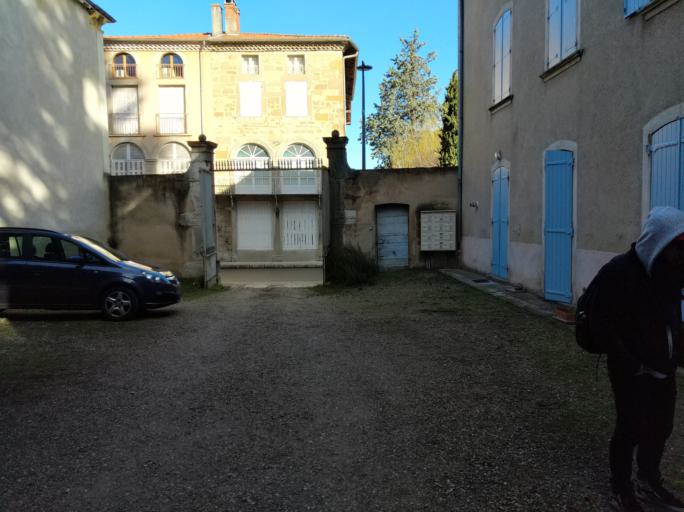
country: FR
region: Rhone-Alpes
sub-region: Departement de la Drome
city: Saint-Sorlin-en-Valloire
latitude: 45.2898
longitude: 4.9919
